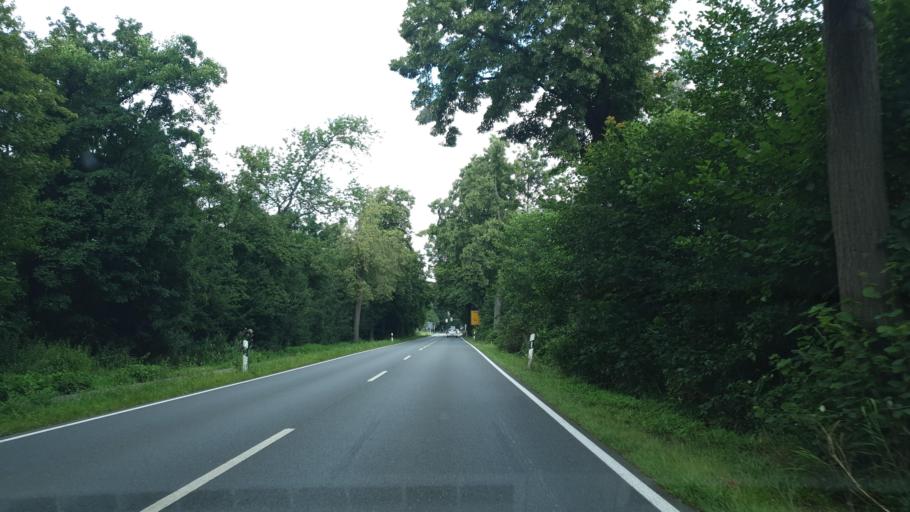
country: DE
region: North Rhine-Westphalia
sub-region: Regierungsbezirk Detmold
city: Guetersloh
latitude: 51.9415
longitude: 8.4255
